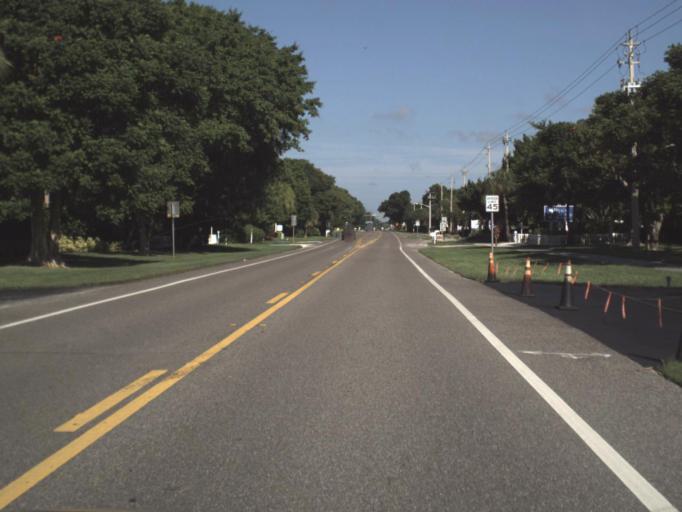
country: US
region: Florida
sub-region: Manatee County
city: Longboat Key
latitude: 27.4087
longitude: -82.6554
